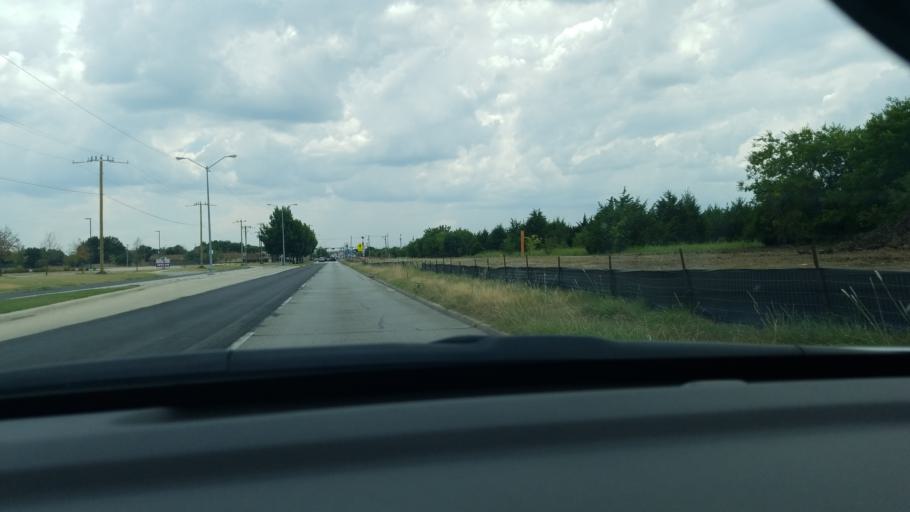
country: US
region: Texas
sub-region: Dallas County
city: Grand Prairie
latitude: 32.6870
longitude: -97.0443
